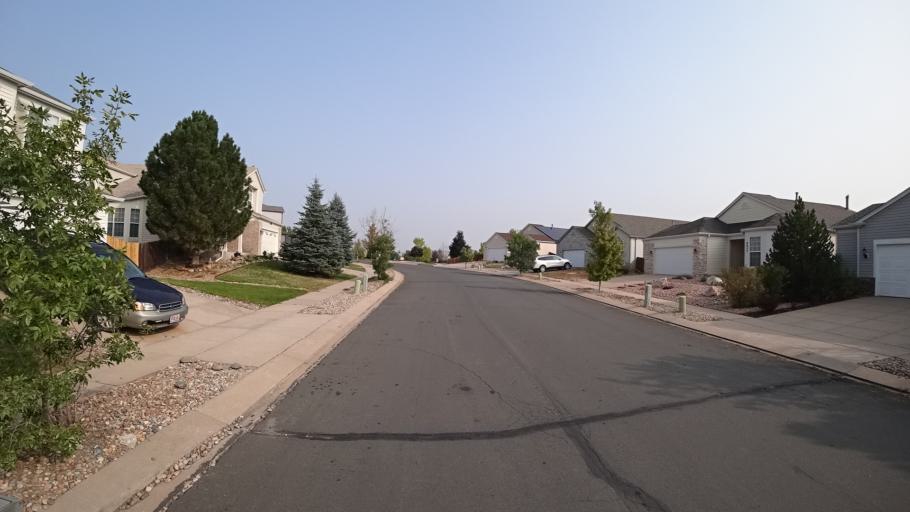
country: US
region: Colorado
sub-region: El Paso County
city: Cimarron Hills
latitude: 38.9312
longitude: -104.7297
